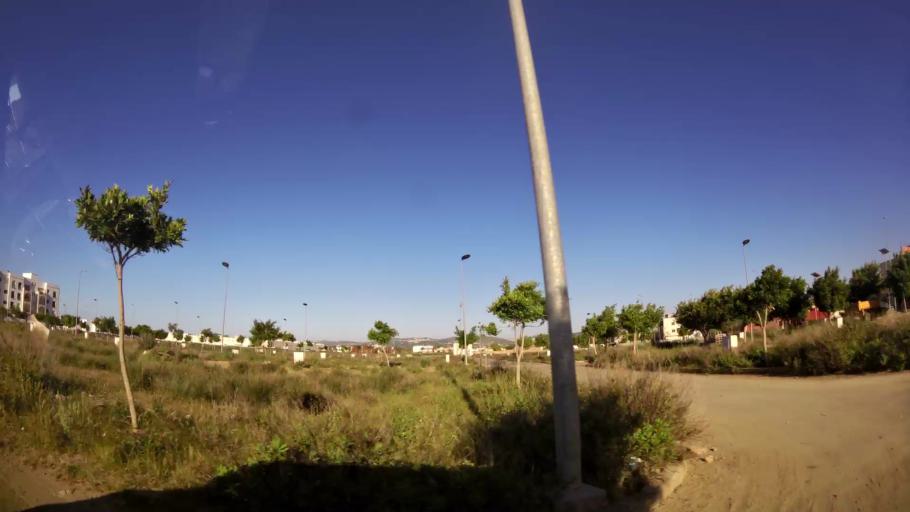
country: MA
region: Oriental
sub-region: Berkane-Taourirt
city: Madagh
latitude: 35.0840
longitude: -2.2542
